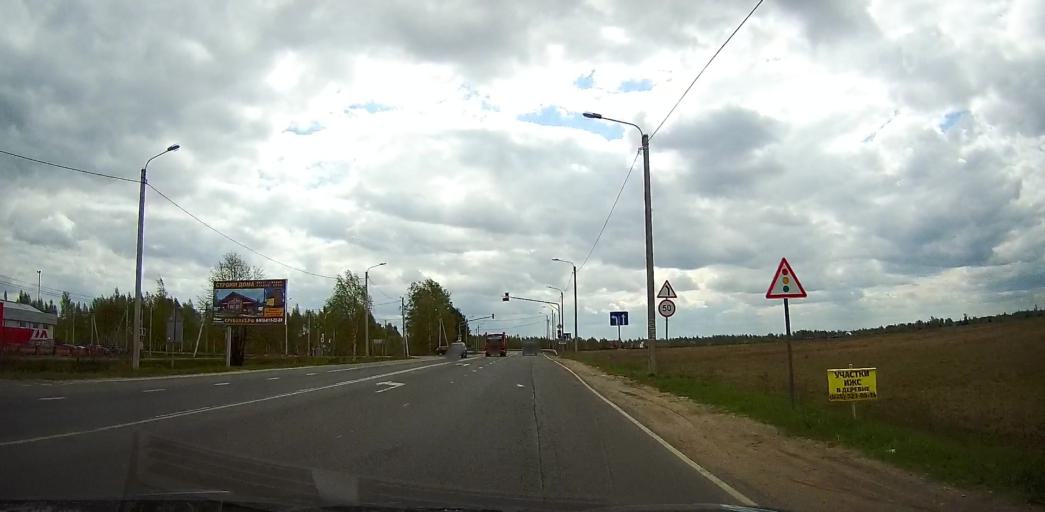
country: RU
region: Moskovskaya
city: Beloozerskiy
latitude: 55.4584
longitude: 38.4246
